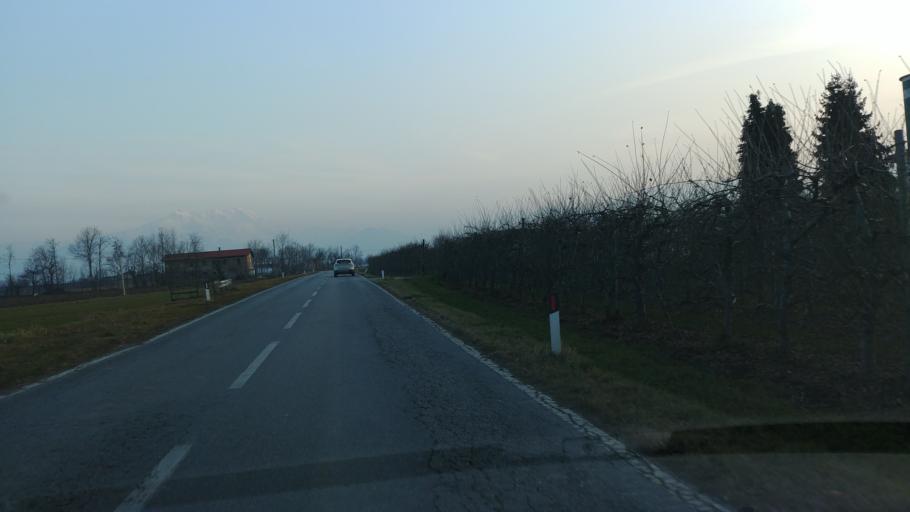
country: IT
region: Piedmont
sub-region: Provincia di Cuneo
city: Roata Rossi
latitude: 44.4223
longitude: 7.5073
